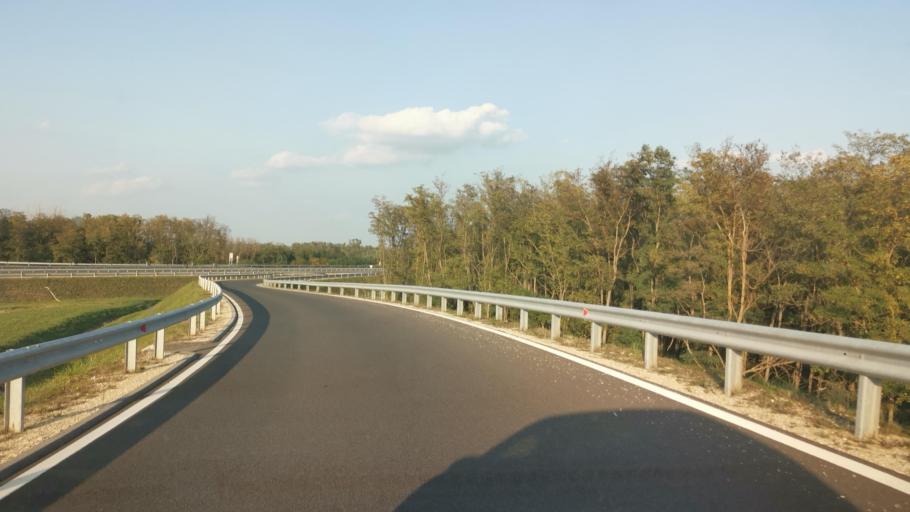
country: HU
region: Gyor-Moson-Sopron
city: Fertoszentmiklos
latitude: 47.5849
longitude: 16.9368
